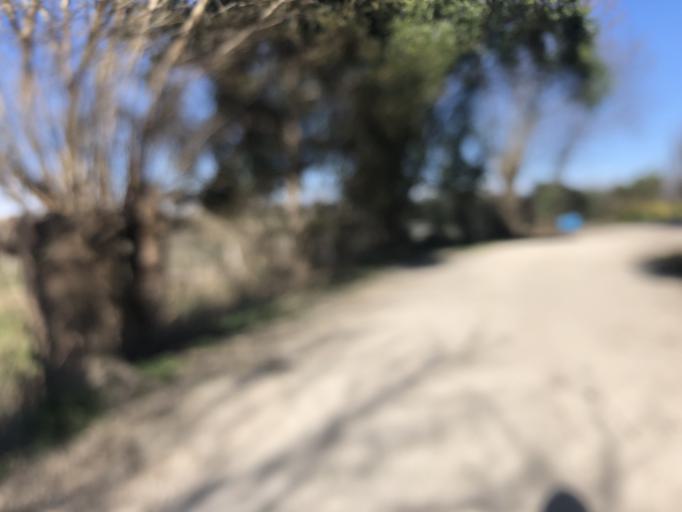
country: IT
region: Veneto
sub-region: Provincia di Verona
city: San Giorgio in Salici
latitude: 45.4278
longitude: 10.8082
